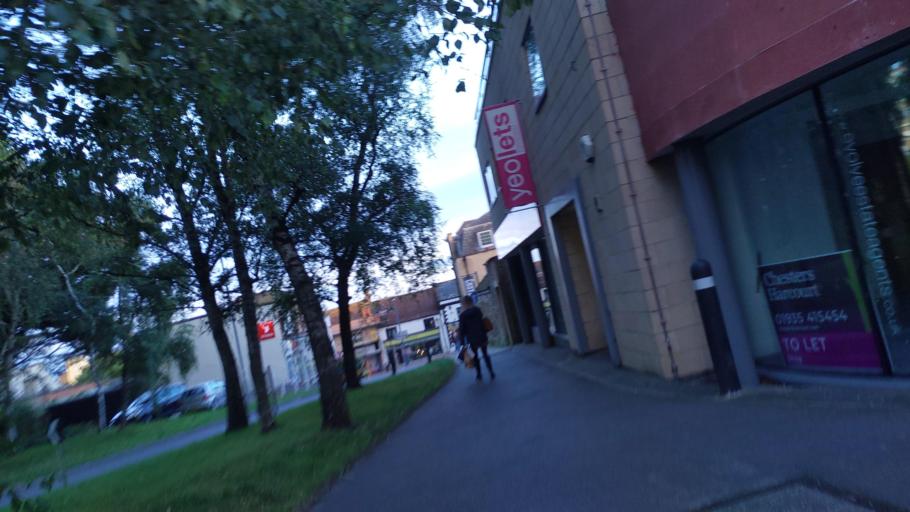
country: GB
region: England
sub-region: Somerset
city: Yeovil
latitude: 50.9428
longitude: -2.6348
